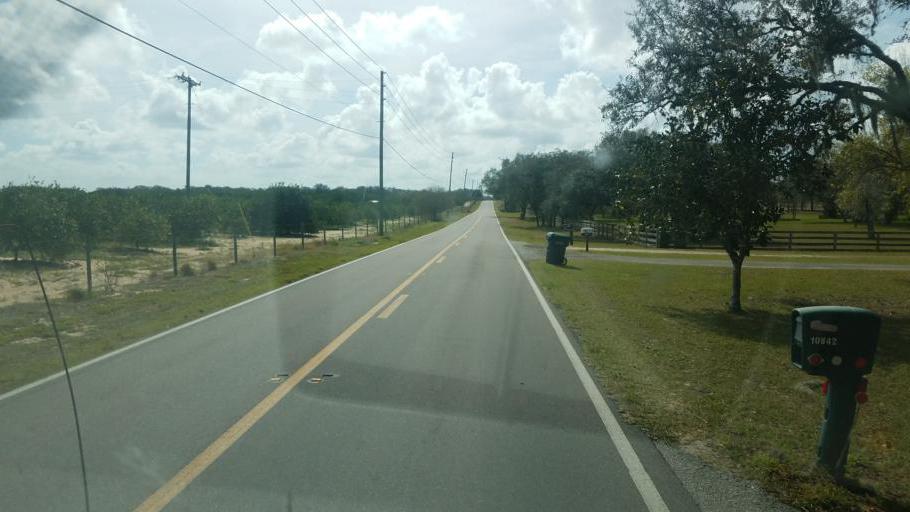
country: US
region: Florida
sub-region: Polk County
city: Dundee
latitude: 28.0471
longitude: -81.5333
